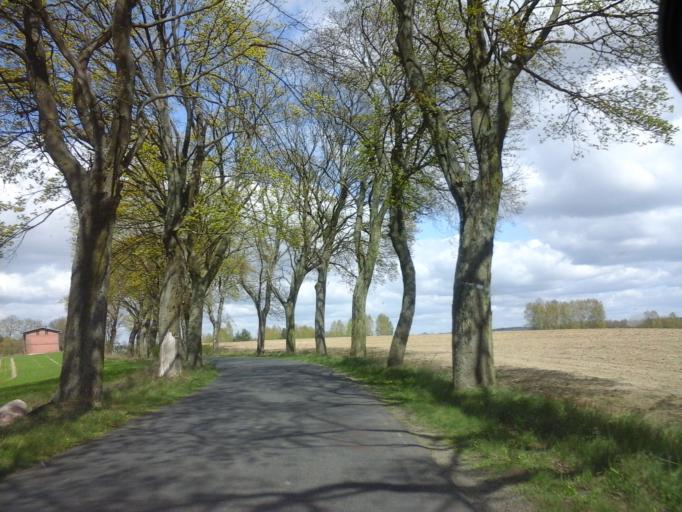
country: PL
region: West Pomeranian Voivodeship
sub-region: Powiat choszczenski
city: Recz
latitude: 53.1711
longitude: 15.6101
